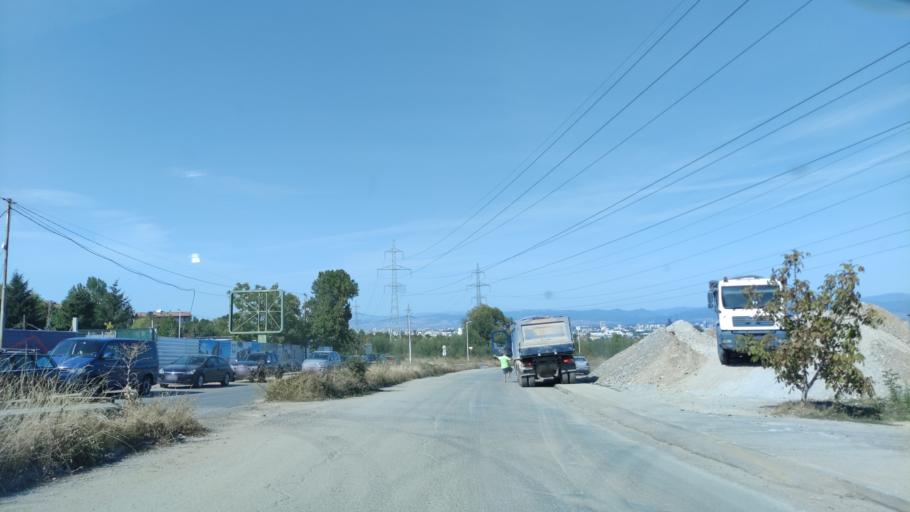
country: BG
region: Sofia-Capital
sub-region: Stolichna Obshtina
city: Sofia
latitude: 42.6210
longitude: 23.3485
